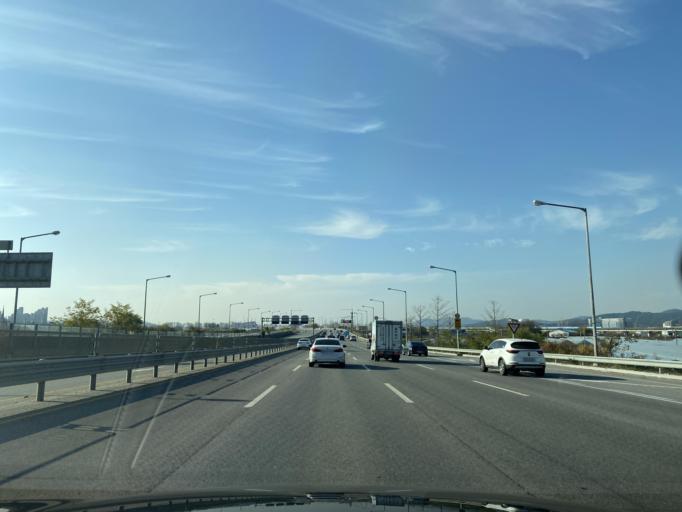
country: KR
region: Chungcheongnam-do
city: Asan
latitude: 36.7779
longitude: 127.0718
